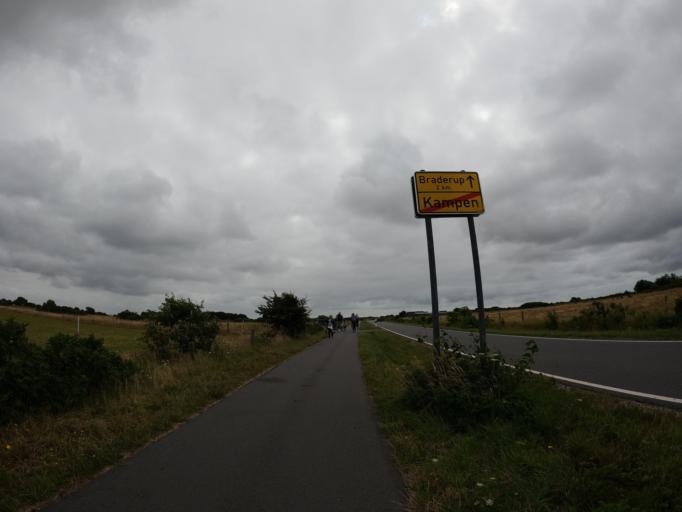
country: DE
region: Schleswig-Holstein
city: Tinnum
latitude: 54.9483
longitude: 8.3470
